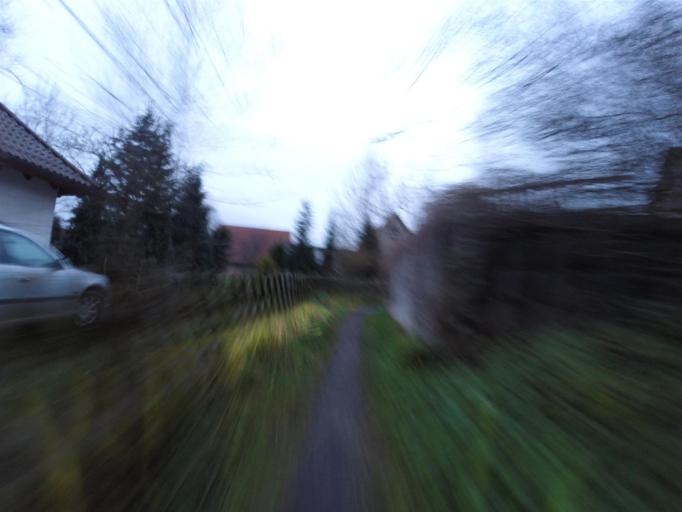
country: DE
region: Thuringia
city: Jena
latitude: 50.9049
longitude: 11.6002
